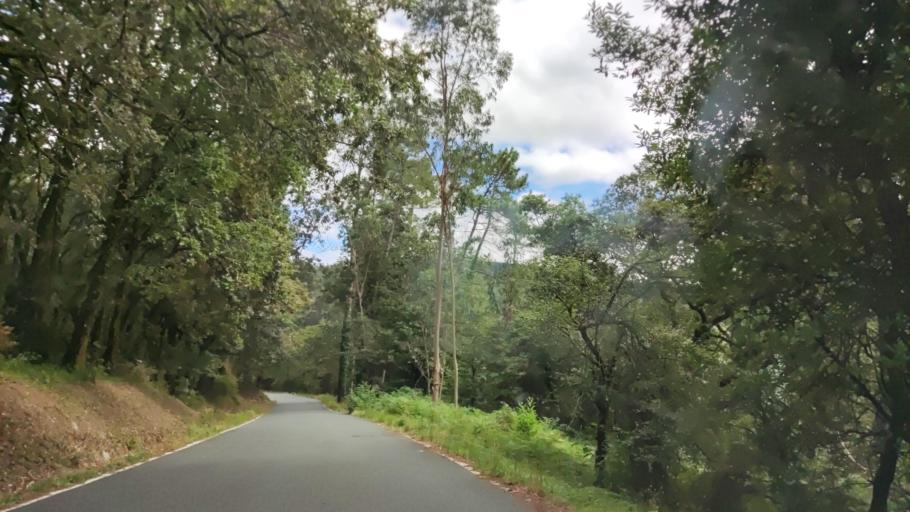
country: ES
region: Galicia
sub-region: Provincia da Coruna
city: Rois
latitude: 42.7372
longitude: -8.7012
